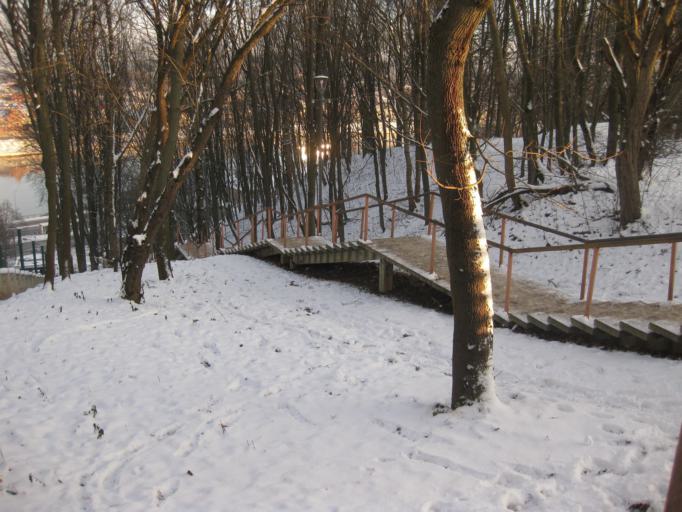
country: LT
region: Kauno apskritis
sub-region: Kaunas
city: Aleksotas
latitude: 54.8909
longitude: 23.8869
